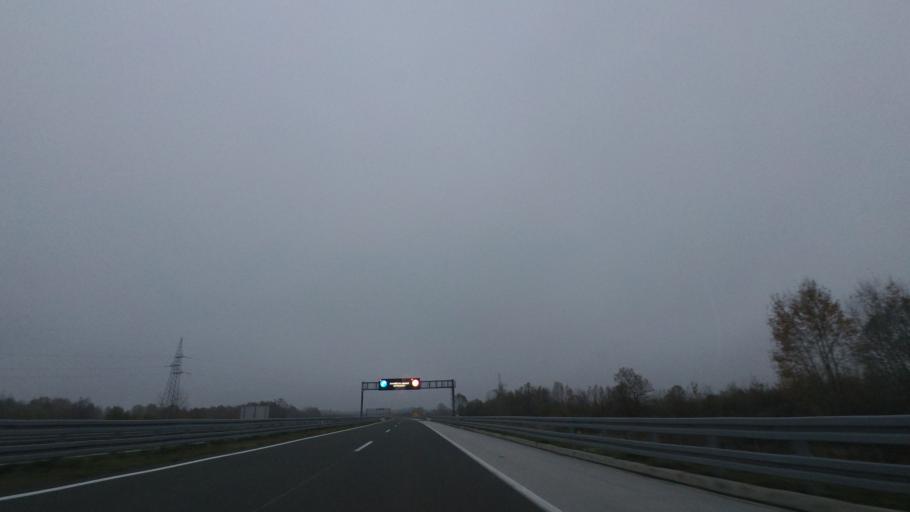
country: HR
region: Sisacko-Moslavacka
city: Lekenik
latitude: 45.5695
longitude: 16.2092
